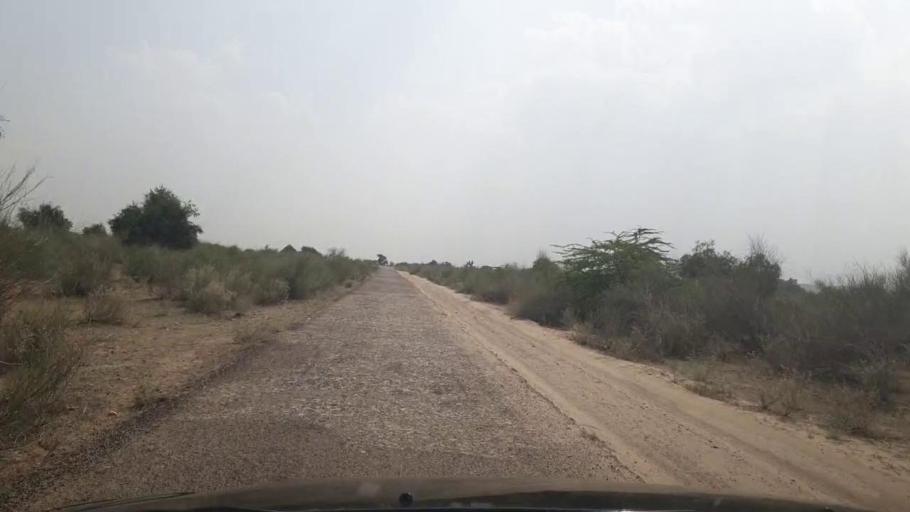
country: PK
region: Sindh
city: Islamkot
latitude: 24.9430
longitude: 70.5722
